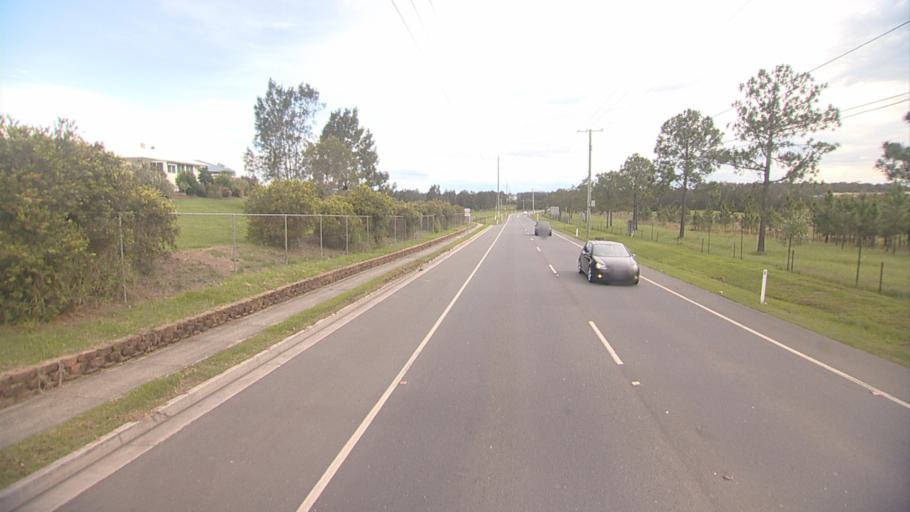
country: AU
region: Queensland
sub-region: Logan
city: Waterford West
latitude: -27.6921
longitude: 153.1195
